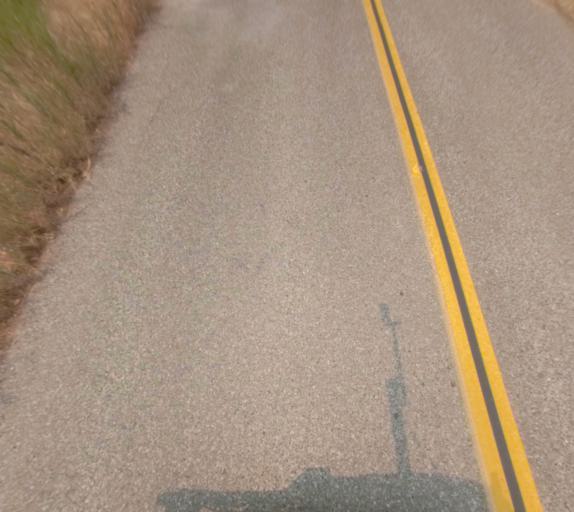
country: US
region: California
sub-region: Madera County
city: Oakhurst
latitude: 37.3266
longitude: -119.6660
